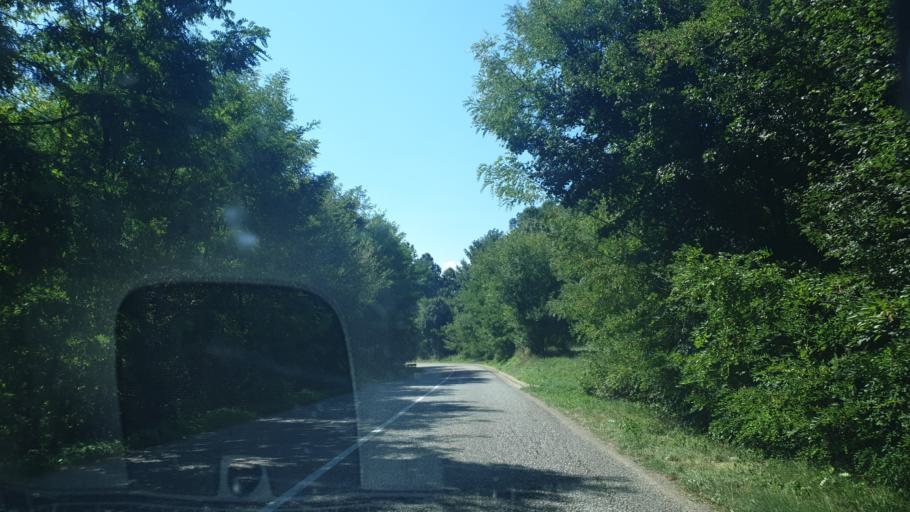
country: RS
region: Central Serbia
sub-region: Kolubarski Okrug
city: Mionica
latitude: 44.2002
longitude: 20.0798
